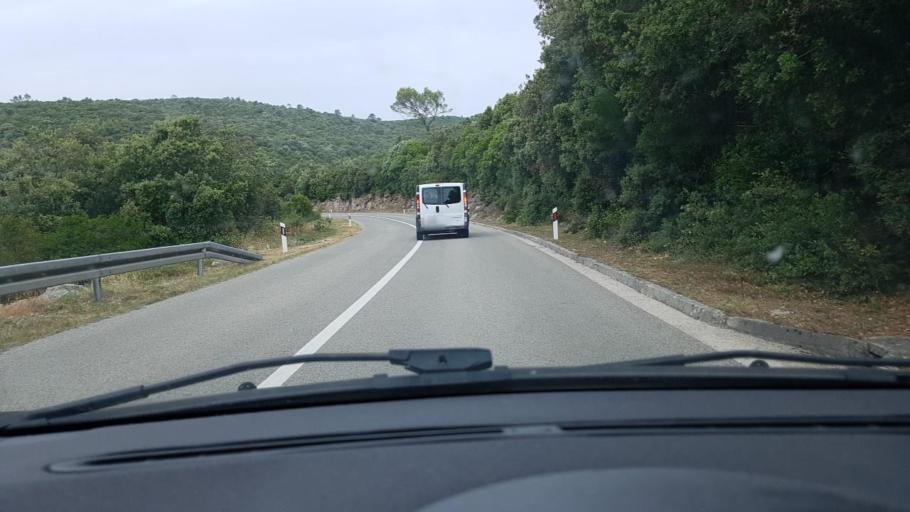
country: HR
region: Dubrovacko-Neretvanska
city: Smokvica
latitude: 42.9470
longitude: 17.0028
